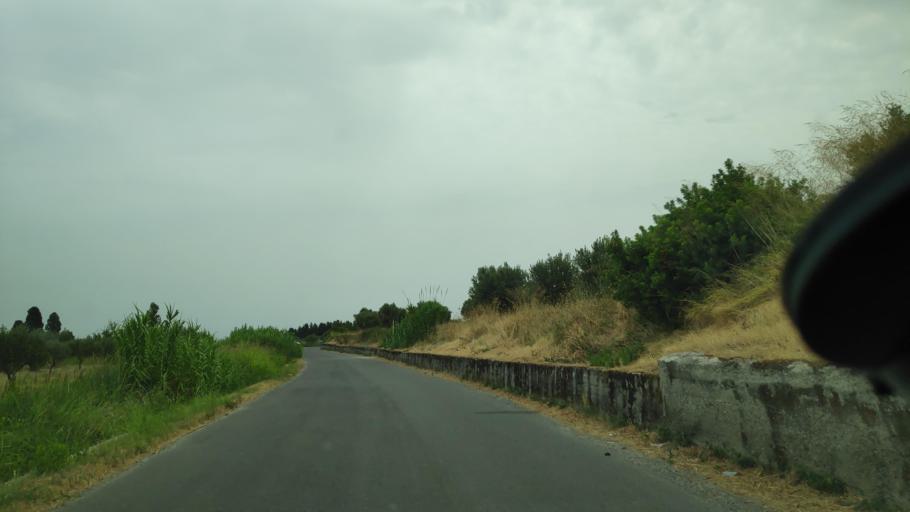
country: IT
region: Calabria
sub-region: Provincia di Catanzaro
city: Martelli-Laganosa
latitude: 38.6657
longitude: 16.5276
